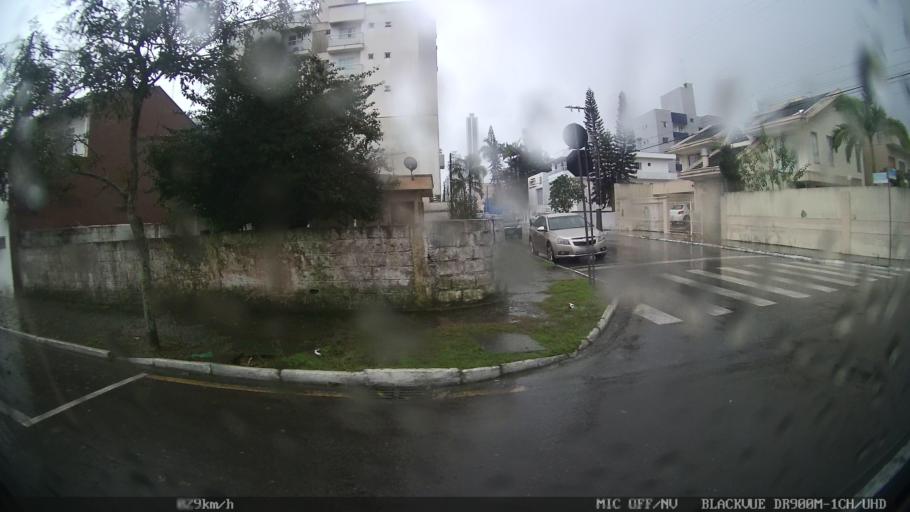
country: BR
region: Santa Catarina
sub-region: Balneario Camboriu
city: Balneario Camboriu
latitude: -27.0080
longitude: -48.6268
